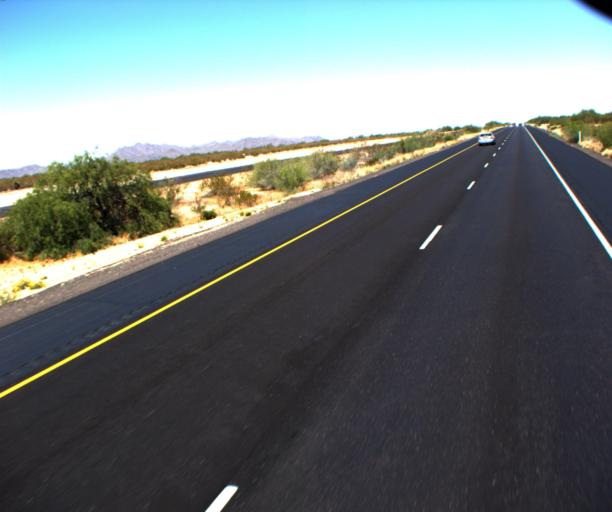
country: US
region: Arizona
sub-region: Yavapai County
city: Congress
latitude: 34.0633
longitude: -112.8642
